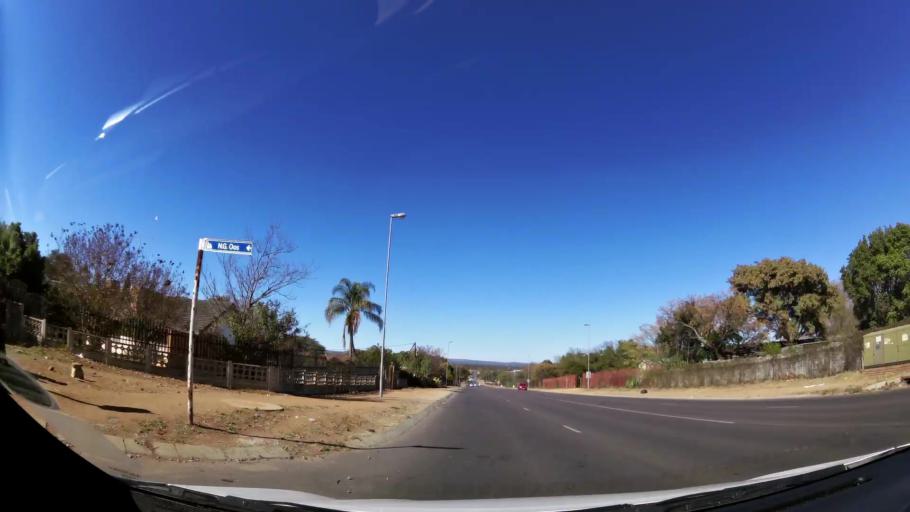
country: ZA
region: Limpopo
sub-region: Capricorn District Municipality
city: Polokwane
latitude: -23.9098
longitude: 29.4744
